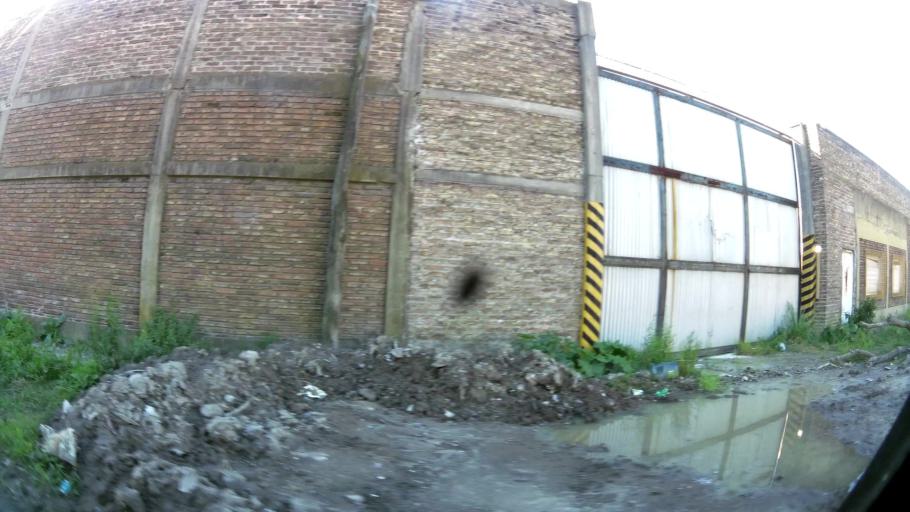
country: AR
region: Buenos Aires
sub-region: Partido de Quilmes
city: Quilmes
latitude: -34.7516
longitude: -58.3166
